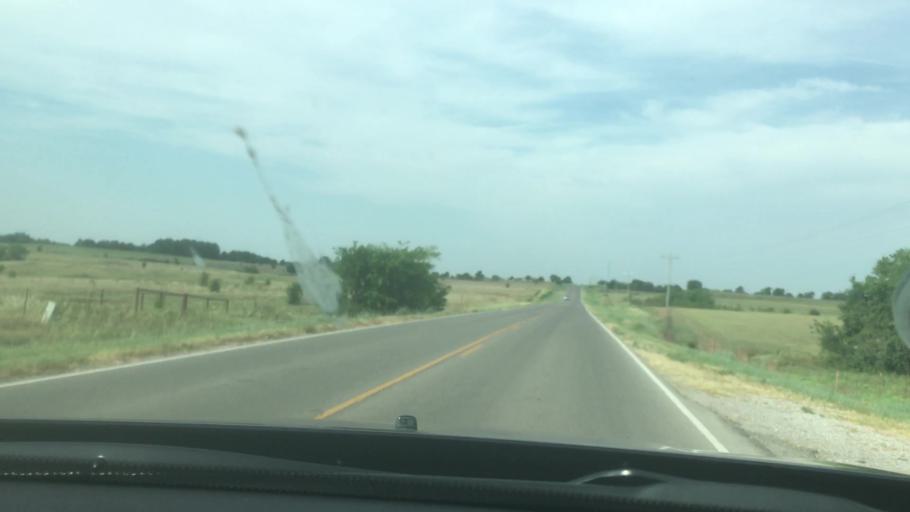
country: US
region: Oklahoma
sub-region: Garvin County
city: Pauls Valley
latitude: 34.7931
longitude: -97.1638
